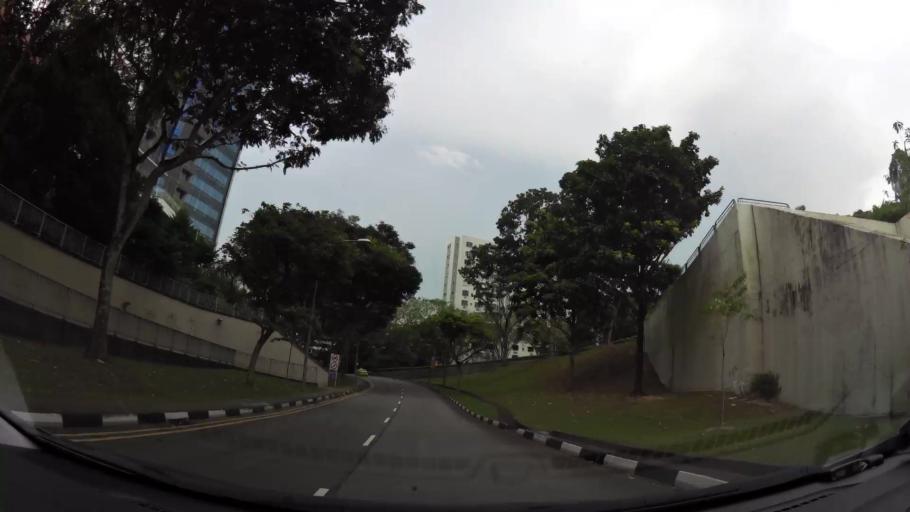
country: SG
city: Singapore
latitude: 1.3069
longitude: 103.8401
